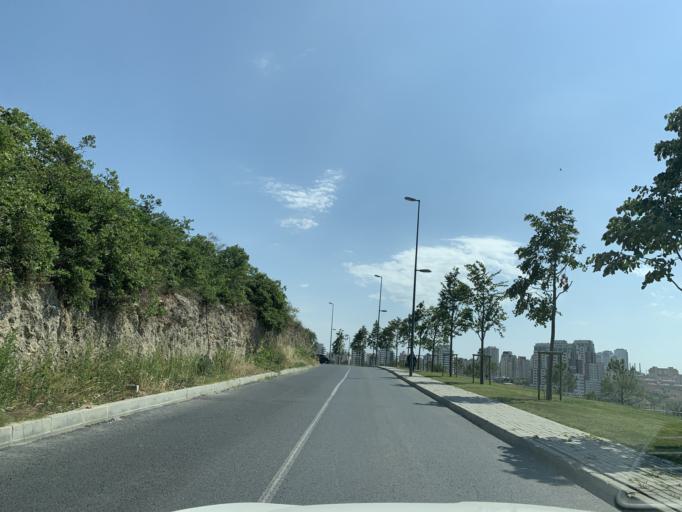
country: TR
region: Istanbul
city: Esenyurt
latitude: 41.0807
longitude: 28.6886
